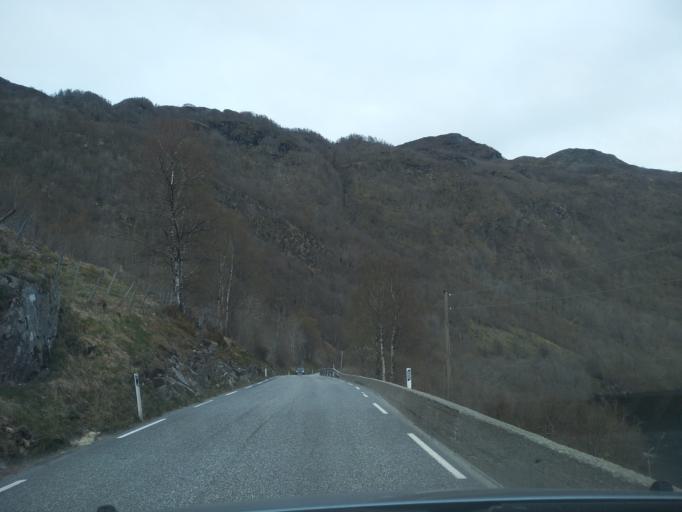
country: NO
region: Hordaland
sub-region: Etne
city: Etne
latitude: 59.7015
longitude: 6.0391
